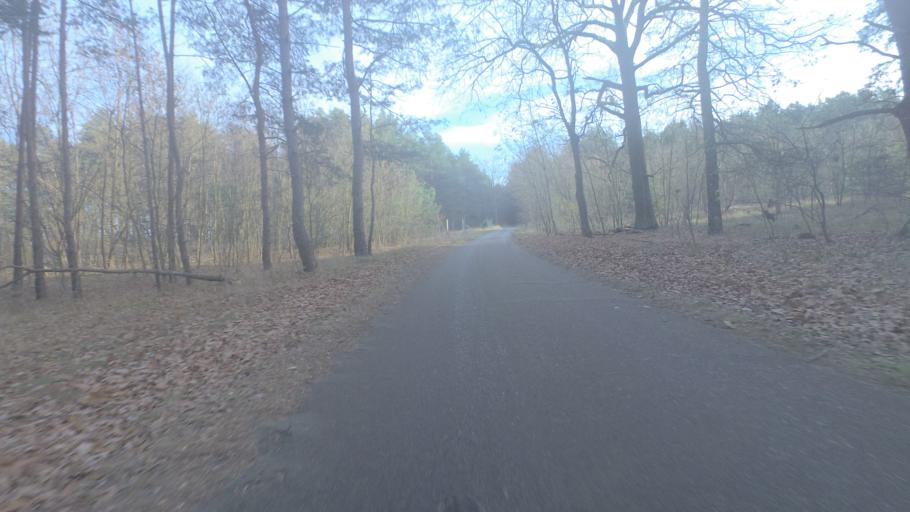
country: DE
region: Brandenburg
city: Zossen
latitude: 52.2199
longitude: 13.4876
